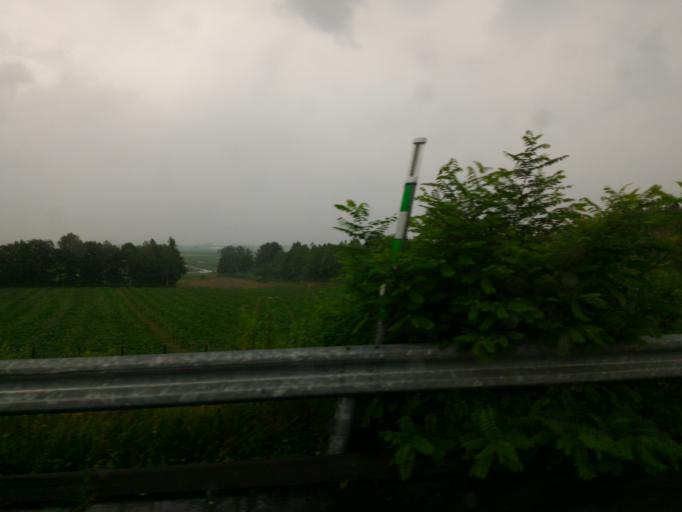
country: JP
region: Hokkaido
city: Nayoro
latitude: 44.4306
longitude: 142.3775
